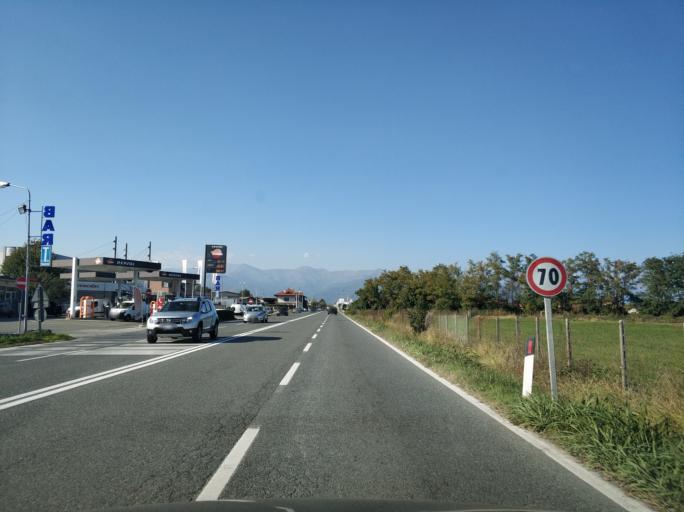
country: IT
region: Piedmont
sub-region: Provincia di Torino
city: Cirie
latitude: 45.2164
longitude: 7.6119
